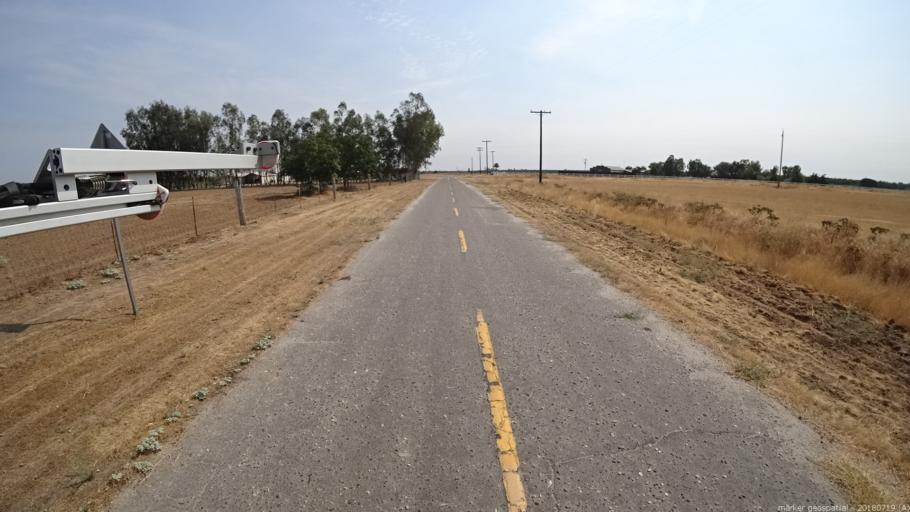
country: US
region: California
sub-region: Madera County
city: Fairmead
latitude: 37.0864
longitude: -120.2079
